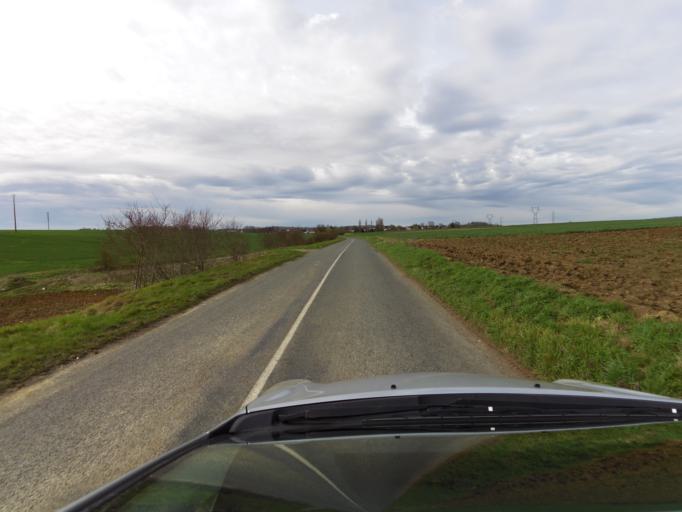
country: FR
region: Picardie
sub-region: Departement de l'Oise
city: Ver-sur-Launette
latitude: 49.0891
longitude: 2.6816
